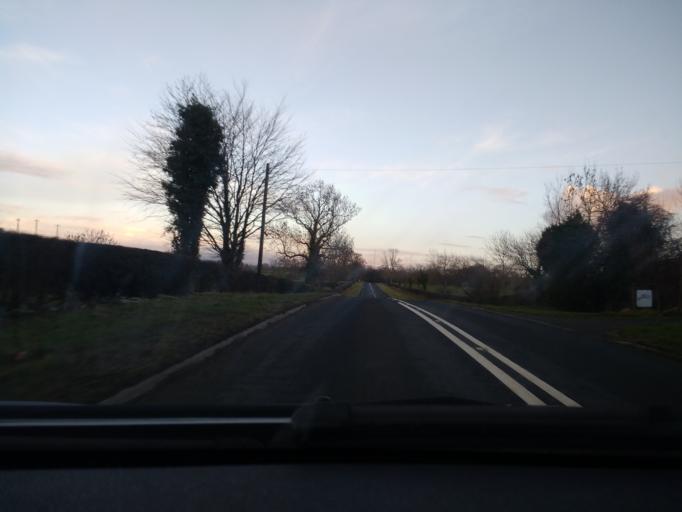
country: GB
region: England
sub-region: Cumbria
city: Scotby
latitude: 54.7293
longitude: -2.9145
